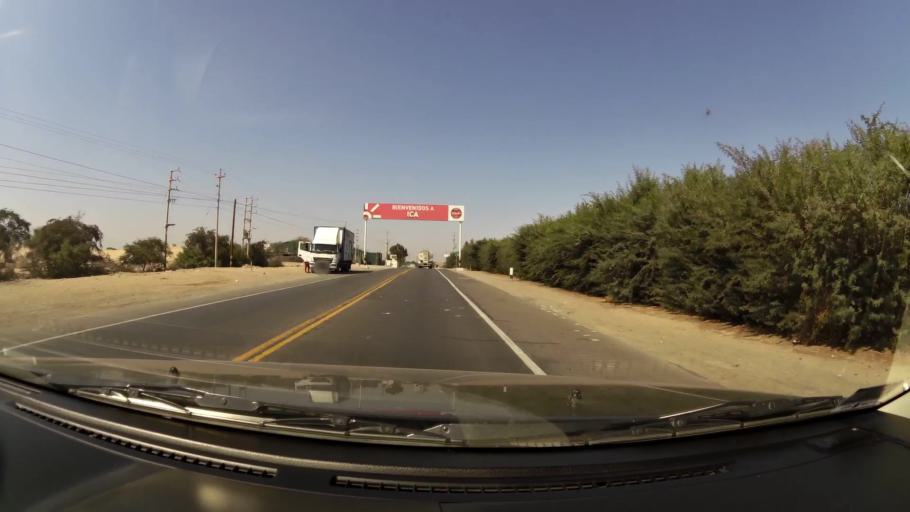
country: PE
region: Ica
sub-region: Provincia de Ica
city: Guadalupe
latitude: -13.9785
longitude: -75.7752
